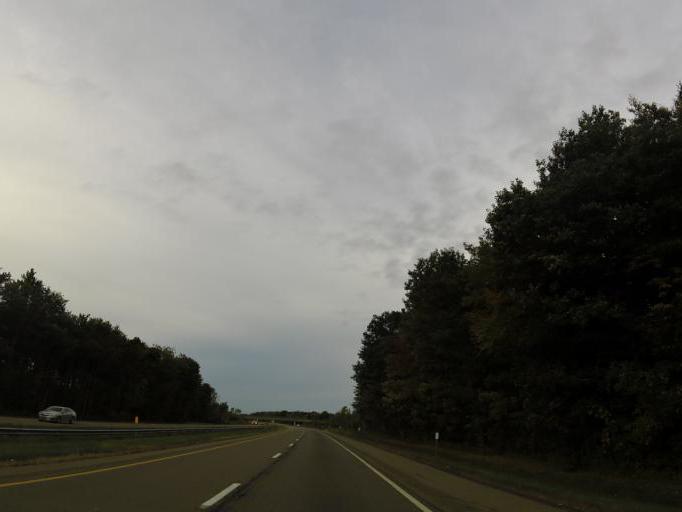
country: US
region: New York
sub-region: Chautauqua County
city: Silver Creek
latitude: 42.4993
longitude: -79.2317
